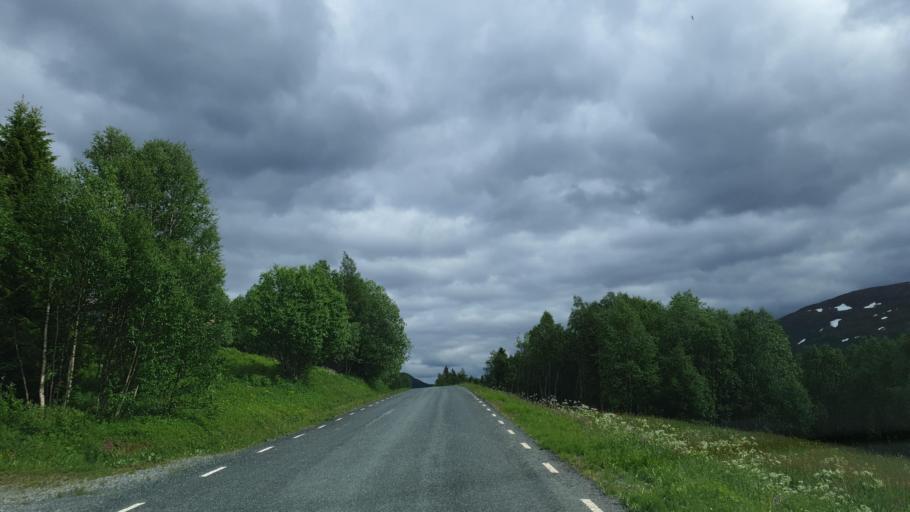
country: NO
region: Nordland
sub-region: Hattfjelldal
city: Hattfjelldal
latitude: 65.4461
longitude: 14.5265
